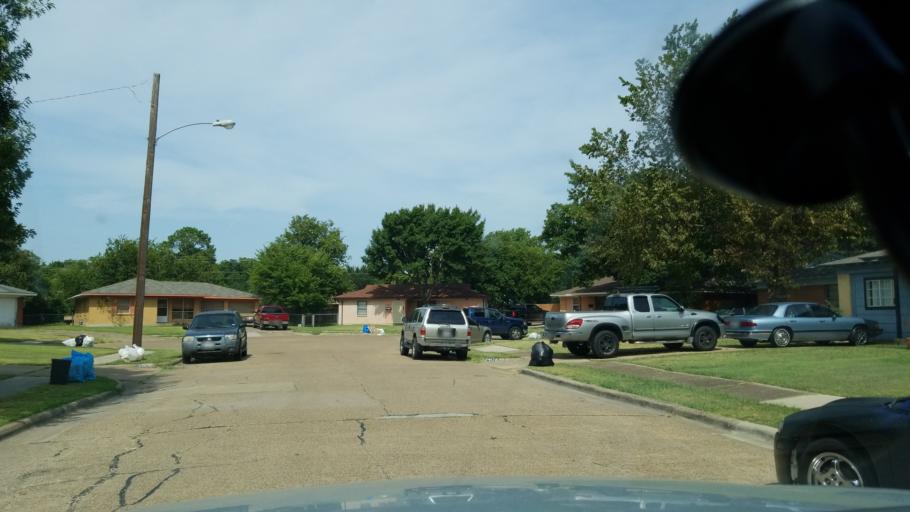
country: US
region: Texas
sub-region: Dallas County
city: Irving
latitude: 32.8193
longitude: -96.9767
